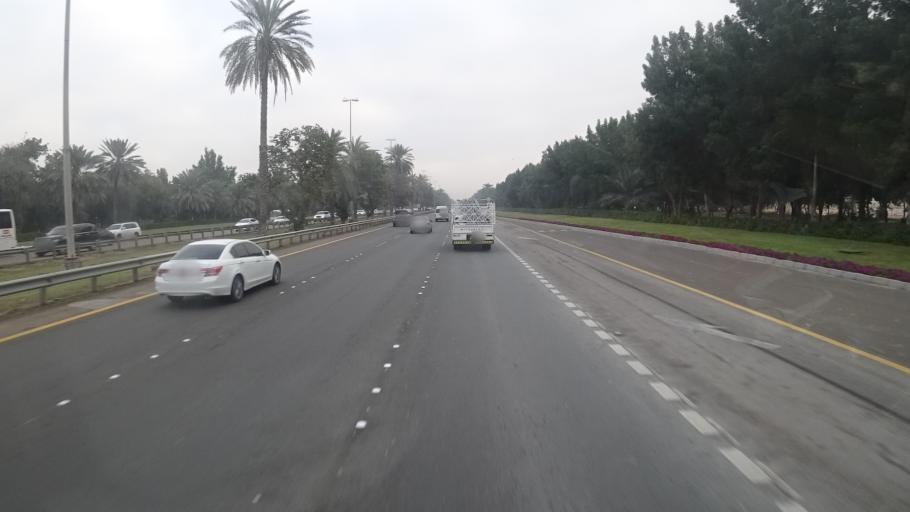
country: AE
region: Abu Dhabi
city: Abu Dhabi
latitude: 24.4024
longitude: 54.5992
